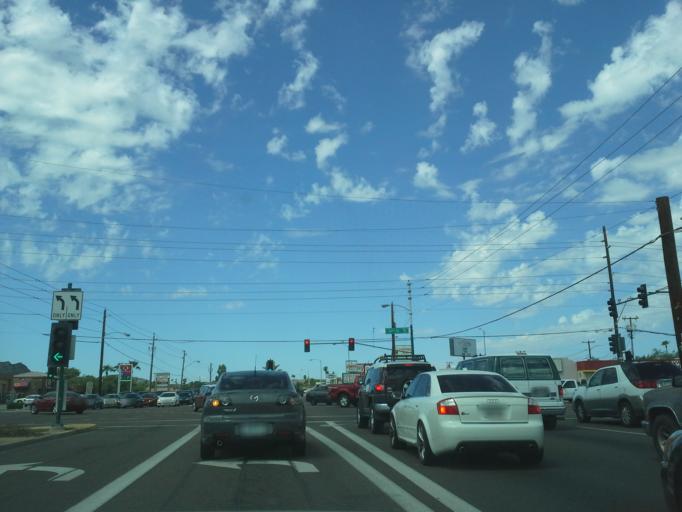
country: US
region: Arizona
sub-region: Maricopa County
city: Paradise Valley
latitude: 33.5970
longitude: -112.0127
